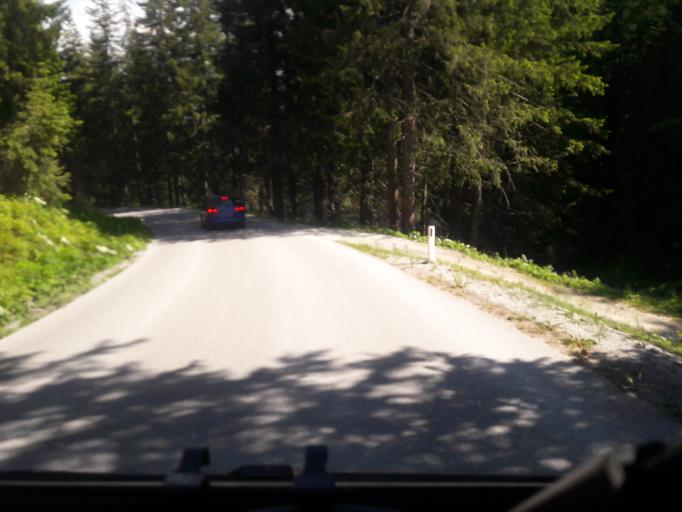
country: AT
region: Styria
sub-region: Politischer Bezirk Liezen
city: Tauplitz
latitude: 47.5831
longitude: 13.9590
